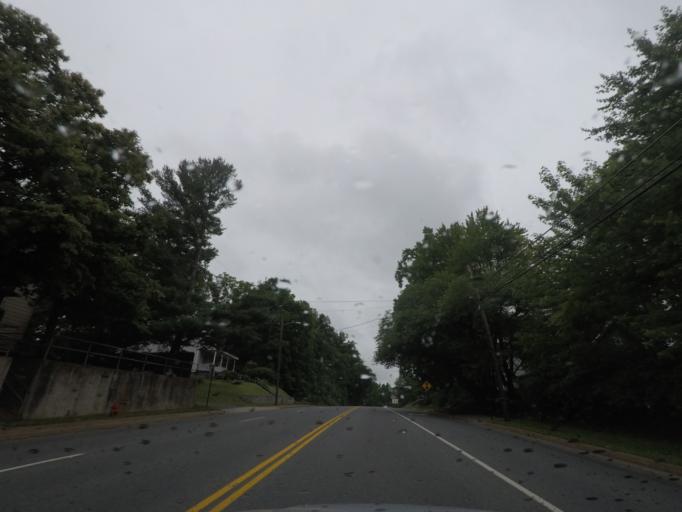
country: US
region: Virginia
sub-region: Orange County
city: Orange
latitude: 38.2373
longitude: -78.1119
